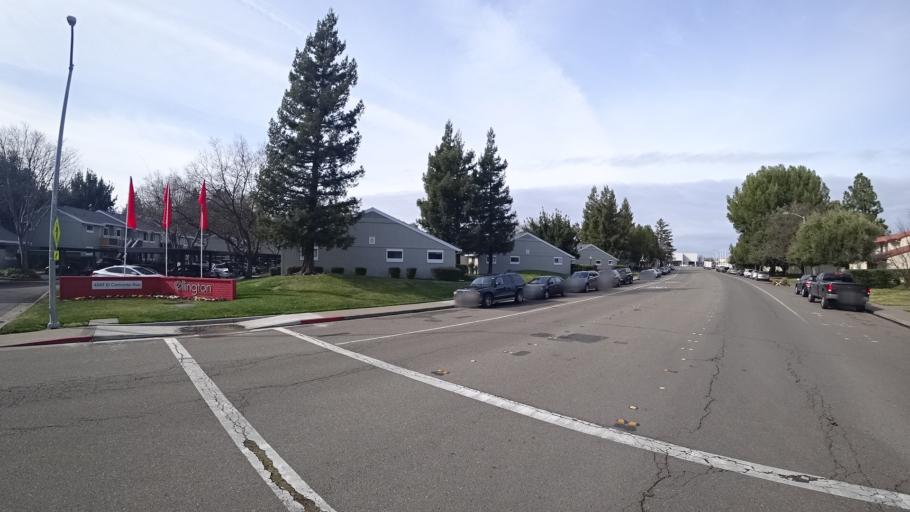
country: US
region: California
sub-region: Yolo County
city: Davis
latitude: 38.5500
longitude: -121.6901
